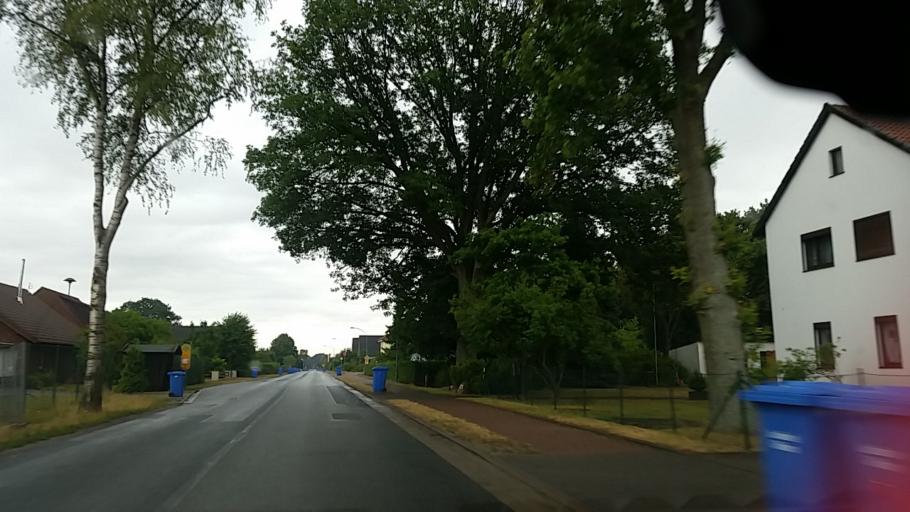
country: DE
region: Lower Saxony
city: Bokensdorf
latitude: 52.5499
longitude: 10.6944
